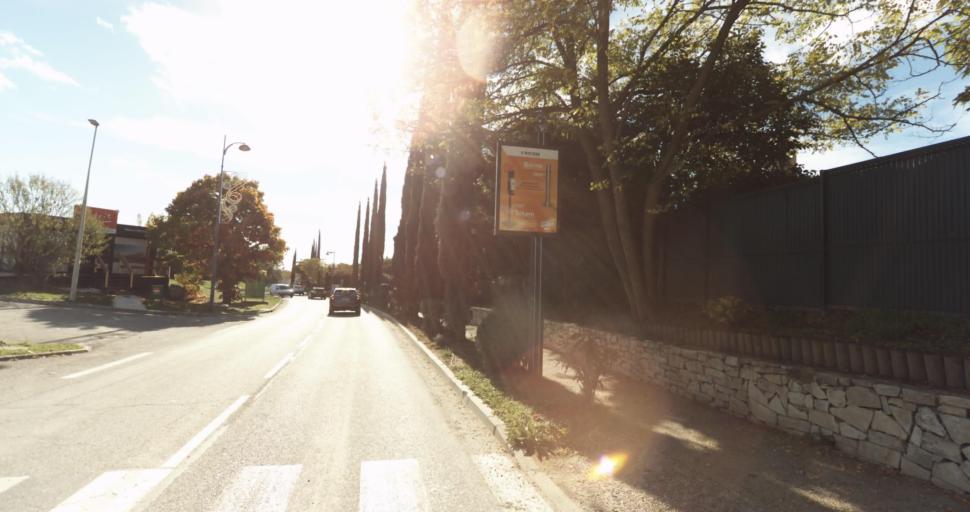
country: FR
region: Provence-Alpes-Cote d'Azur
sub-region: Departement des Bouches-du-Rhone
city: Venelles
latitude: 43.5948
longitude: 5.4826
